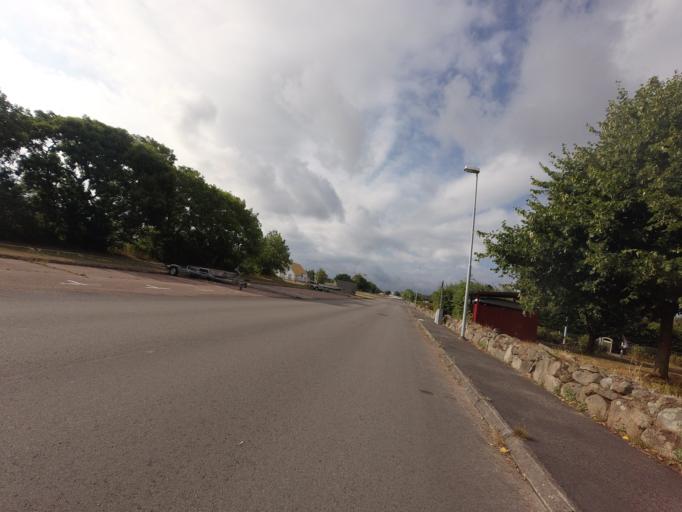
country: SE
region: Skane
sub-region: Hoganas Kommun
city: Hoganas
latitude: 56.1588
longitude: 12.5774
